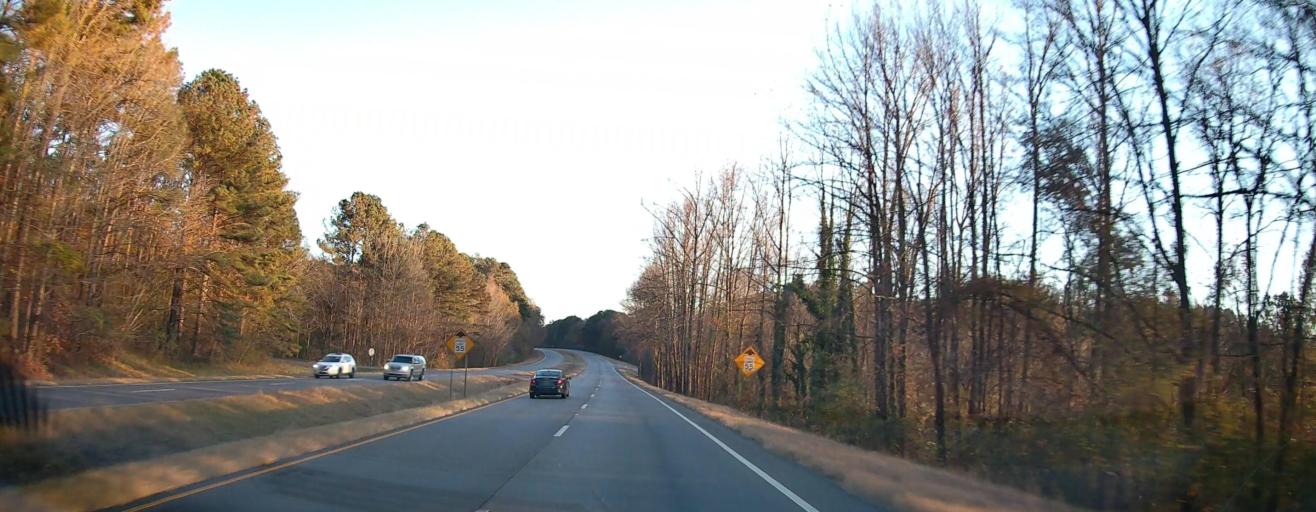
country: US
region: Alabama
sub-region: Etowah County
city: Attalla
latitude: 34.0262
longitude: -86.1101
